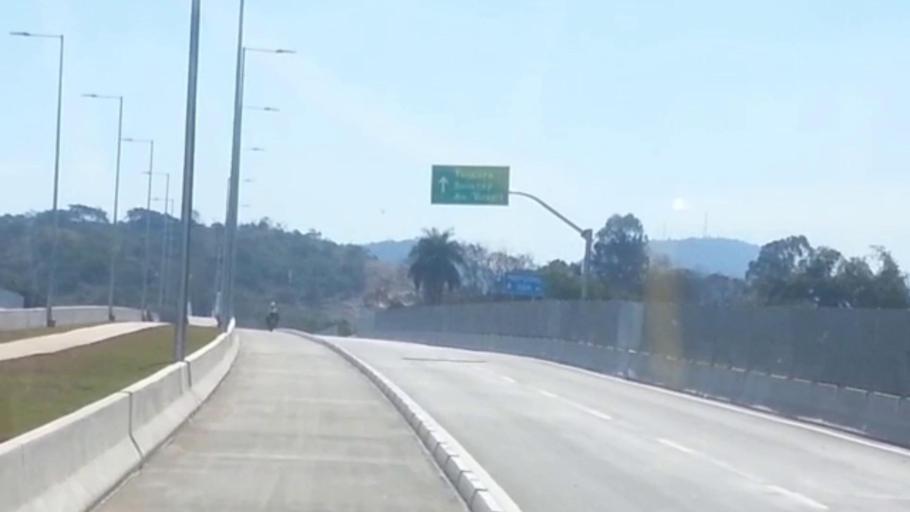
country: BR
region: Rio de Janeiro
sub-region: Nilopolis
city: Nilopolis
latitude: -22.9397
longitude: -43.3947
